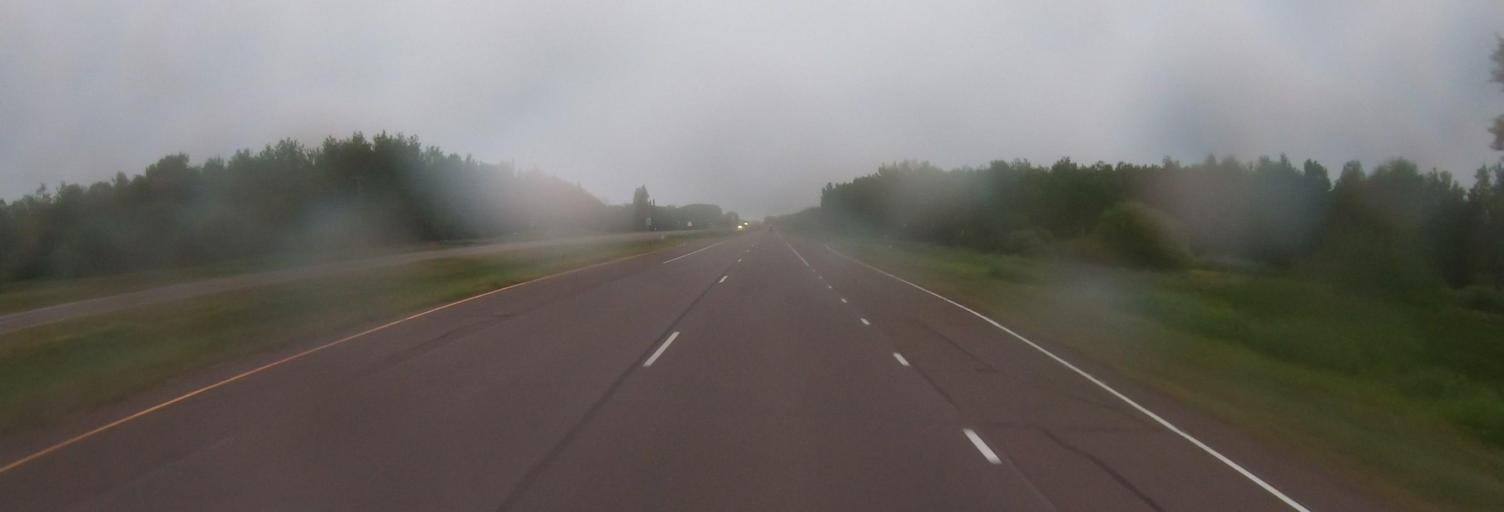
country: US
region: Minnesota
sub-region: Carlton County
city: Cloquet
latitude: 46.9011
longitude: -92.4699
